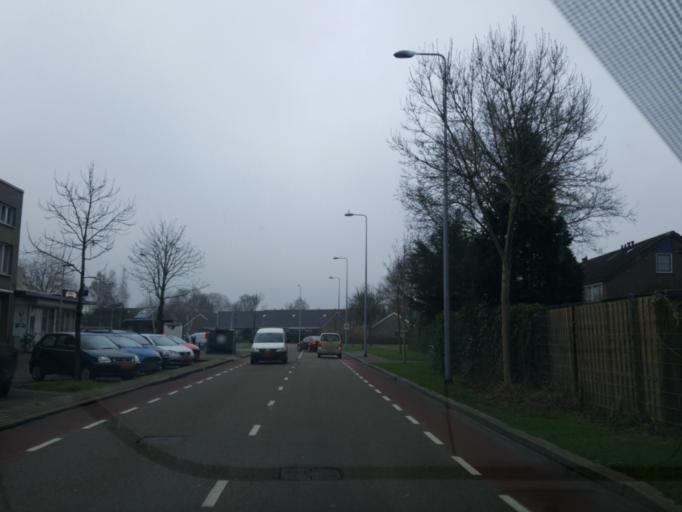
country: NL
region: North Holland
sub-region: Gemeente Bussum
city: Bussum
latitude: 52.2706
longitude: 5.1384
